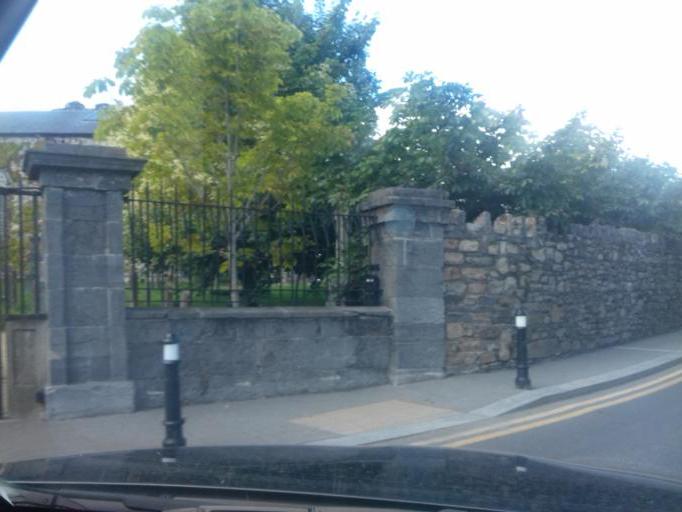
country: IE
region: Leinster
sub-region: Kilkenny
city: Thomastown
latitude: 52.5258
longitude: -7.1390
